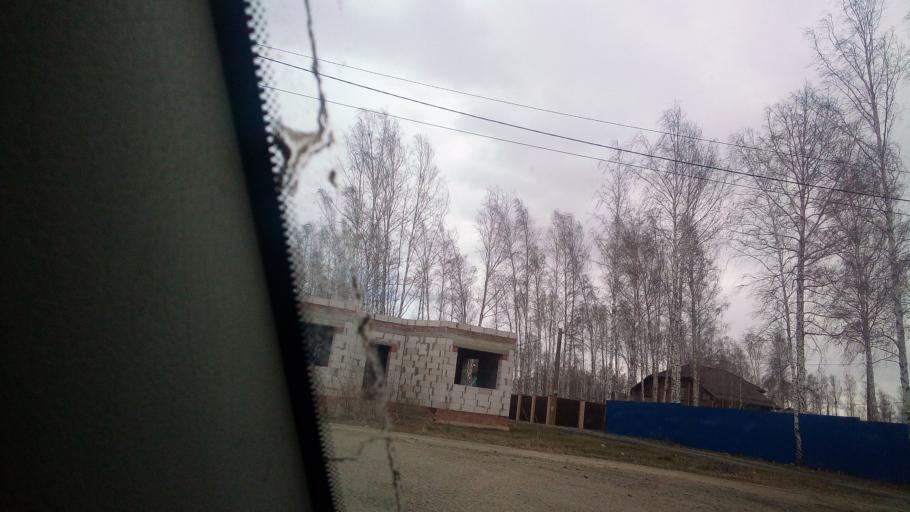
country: RU
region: Chelyabinsk
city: Sargazy
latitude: 55.1288
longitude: 61.2408
